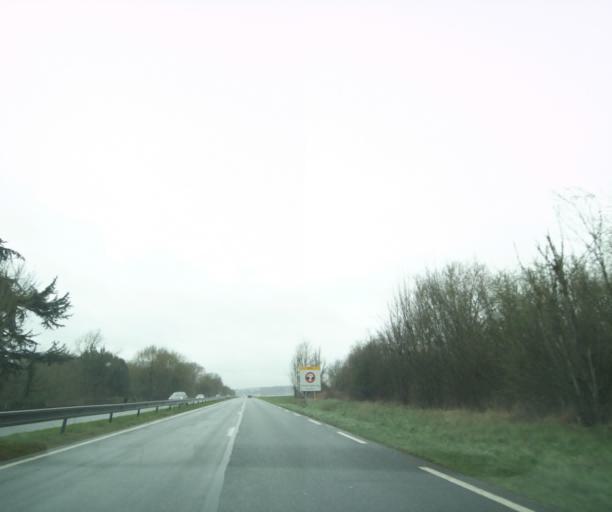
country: FR
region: Ile-de-France
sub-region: Departement de l'Essonne
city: Morigny-Champigny
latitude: 48.4705
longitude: 2.1854
